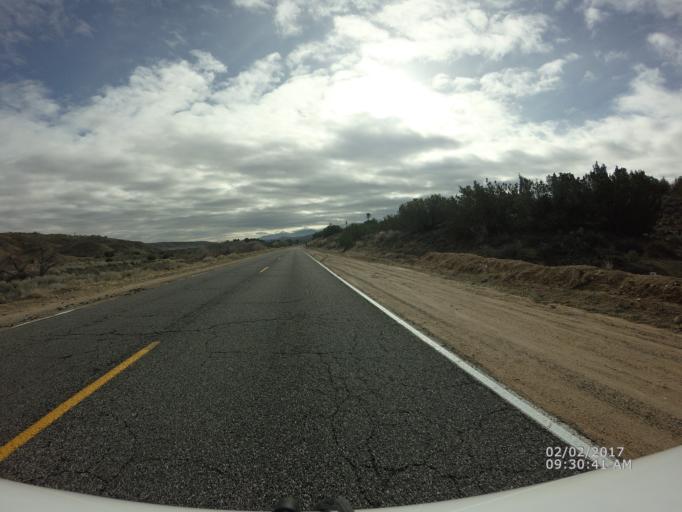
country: US
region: California
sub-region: Los Angeles County
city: Littlerock
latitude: 34.5190
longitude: -118.0386
